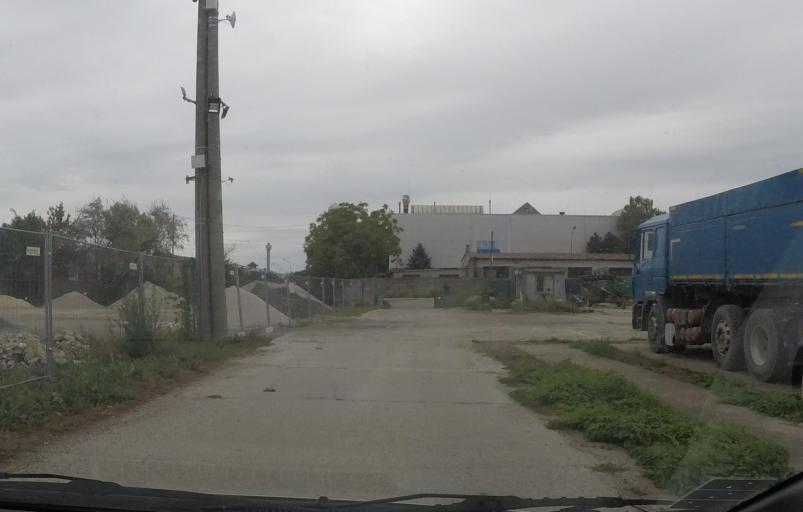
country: SK
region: Trnavsky
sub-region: Okres Galanta
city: Galanta
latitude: 48.1994
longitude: 17.7376
